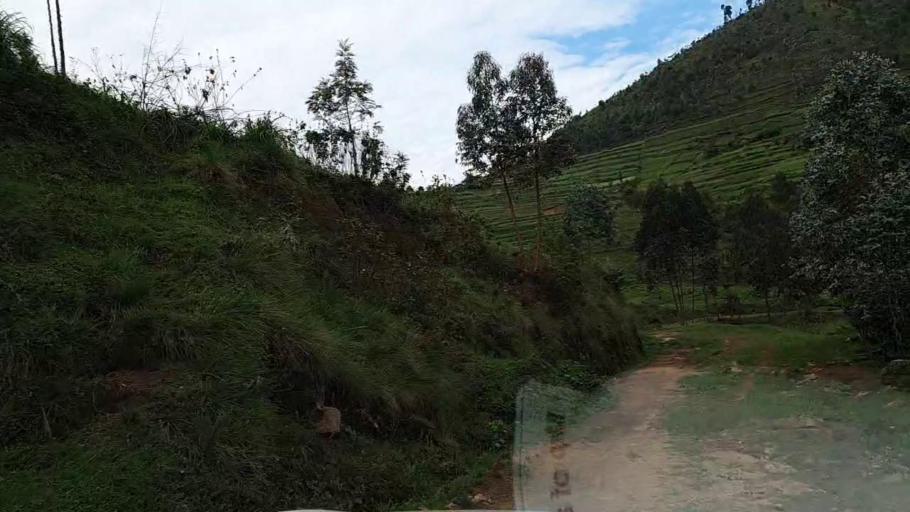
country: RW
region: Southern Province
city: Nzega
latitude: -2.4052
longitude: 29.4986
